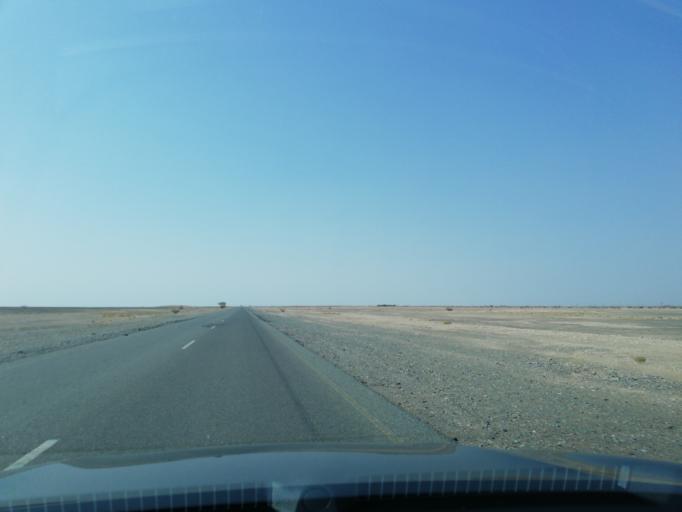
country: OM
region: Muhafazat ad Dakhiliyah
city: Adam
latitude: 22.2748
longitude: 58.0849
